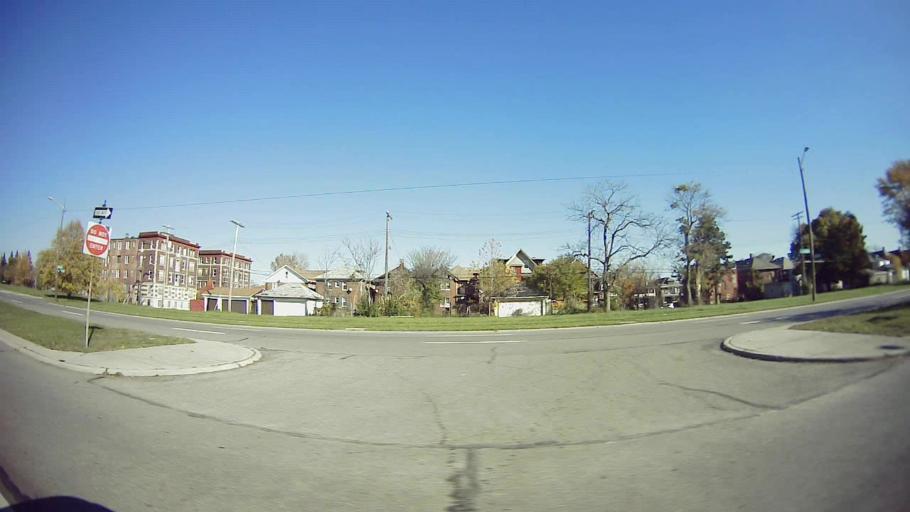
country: US
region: Michigan
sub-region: Wayne County
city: Highland Park
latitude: 42.3657
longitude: -83.0922
